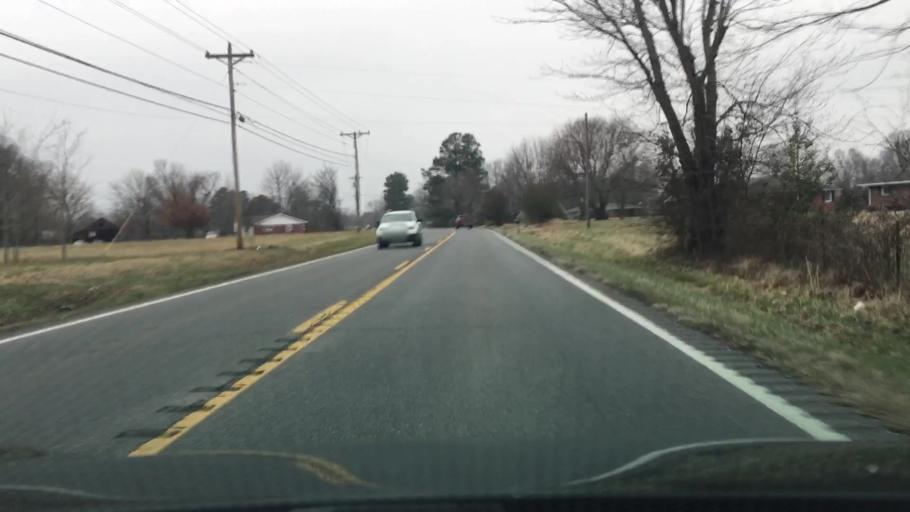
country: US
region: Kentucky
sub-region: Marshall County
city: Calvert City
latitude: 36.9710
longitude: -88.3911
